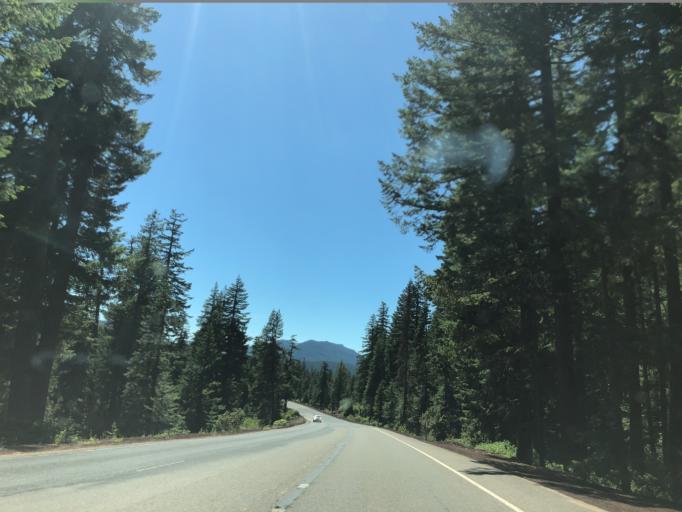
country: US
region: Oregon
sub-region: Deschutes County
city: Sisters
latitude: 44.4327
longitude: -121.9663
